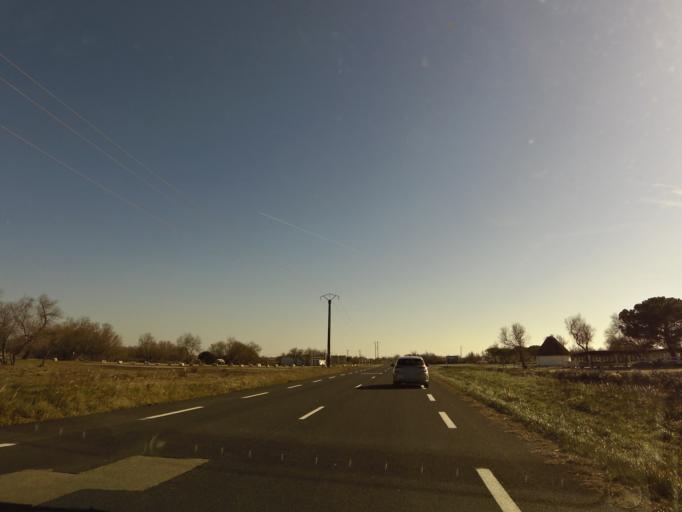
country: FR
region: Languedoc-Roussillon
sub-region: Departement du Gard
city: Aigues-Mortes
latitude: 43.5622
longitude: 4.3161
